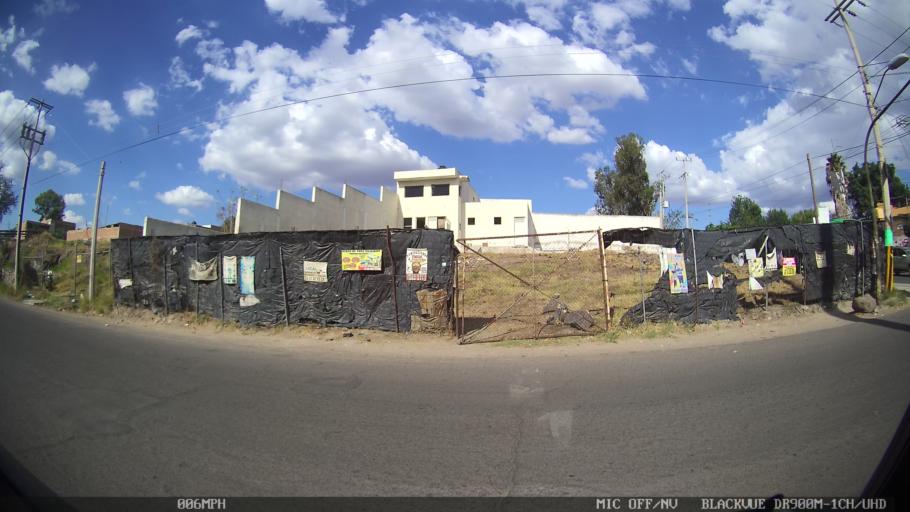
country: MX
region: Jalisco
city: Tlaquepaque
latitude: 20.6575
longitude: -103.2677
